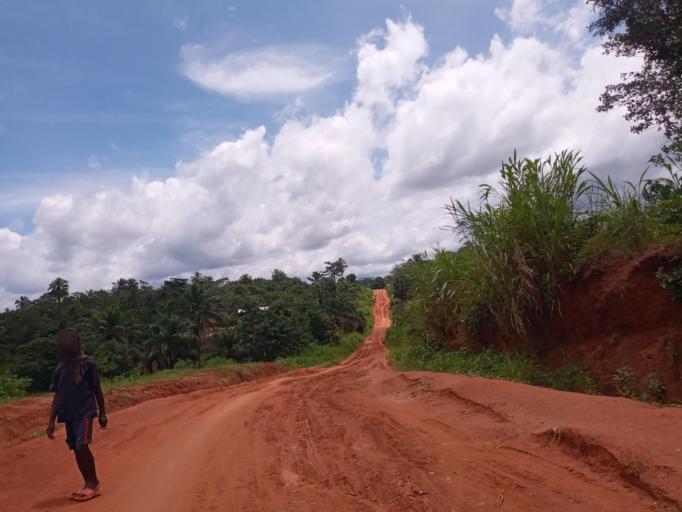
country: SL
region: Eastern Province
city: Koidu
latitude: 8.6446
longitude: -10.9122
